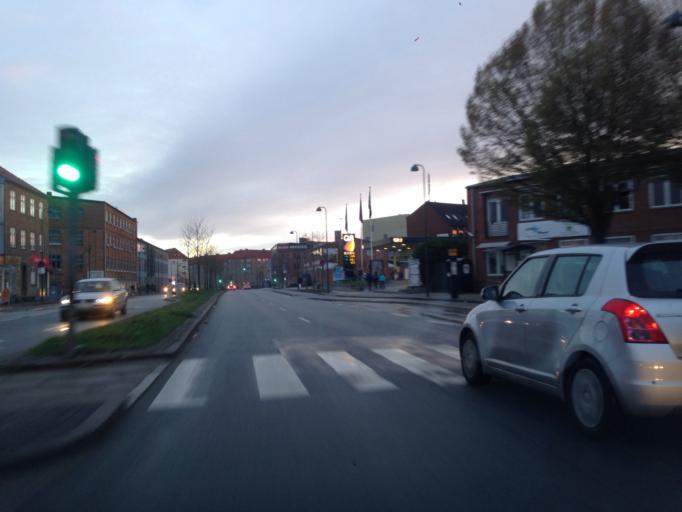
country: DK
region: Capital Region
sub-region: Frederiksberg Kommune
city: Frederiksberg
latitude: 55.7091
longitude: 12.5260
